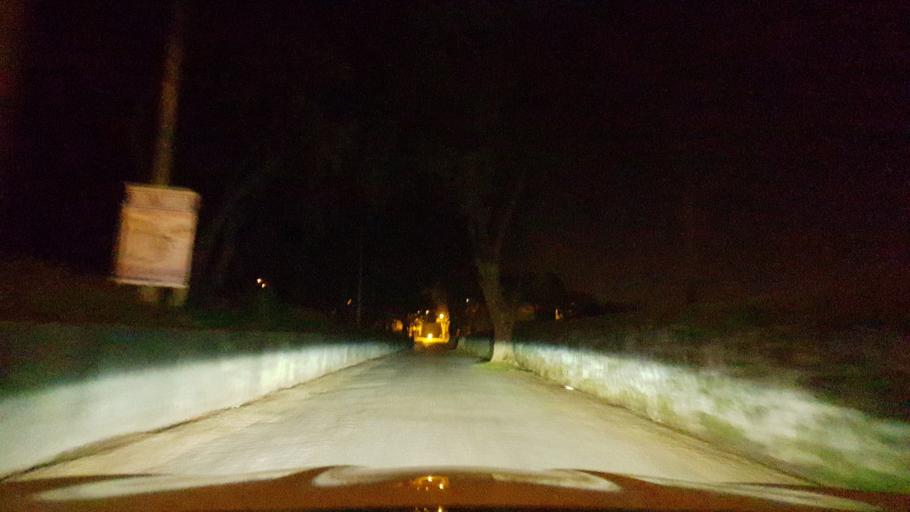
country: PT
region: Porto
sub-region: Matosinhos
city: Guifoes
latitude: 41.2194
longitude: -8.6651
